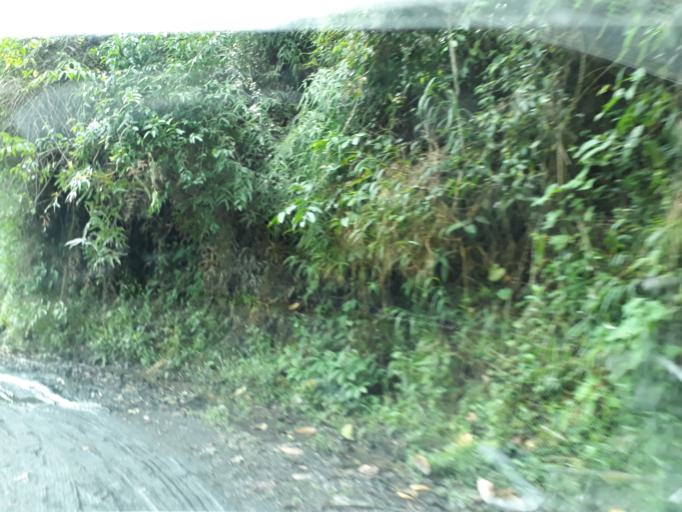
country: CO
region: Cundinamarca
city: Pacho
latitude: 5.1683
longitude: -74.2411
